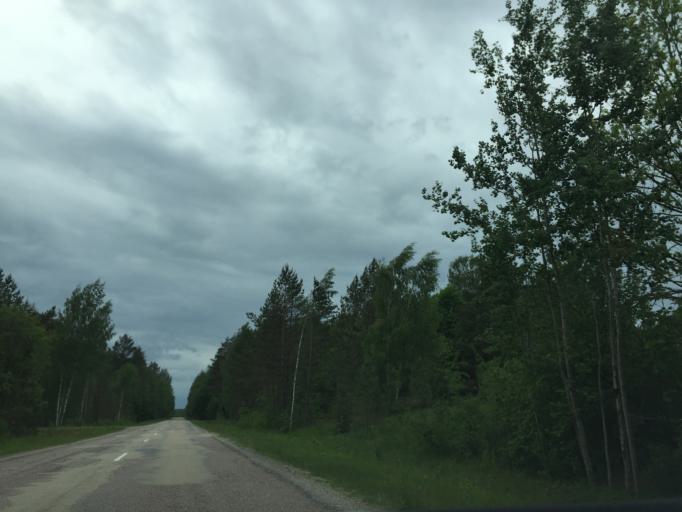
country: LV
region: Aglona
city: Aglona
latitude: 56.1476
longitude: 27.1894
